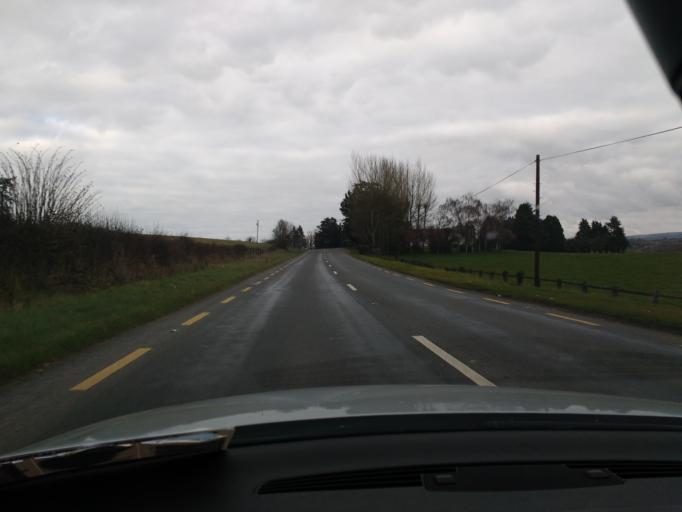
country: IE
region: Leinster
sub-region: Kilkenny
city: Kilkenny
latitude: 52.6794
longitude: -7.2752
